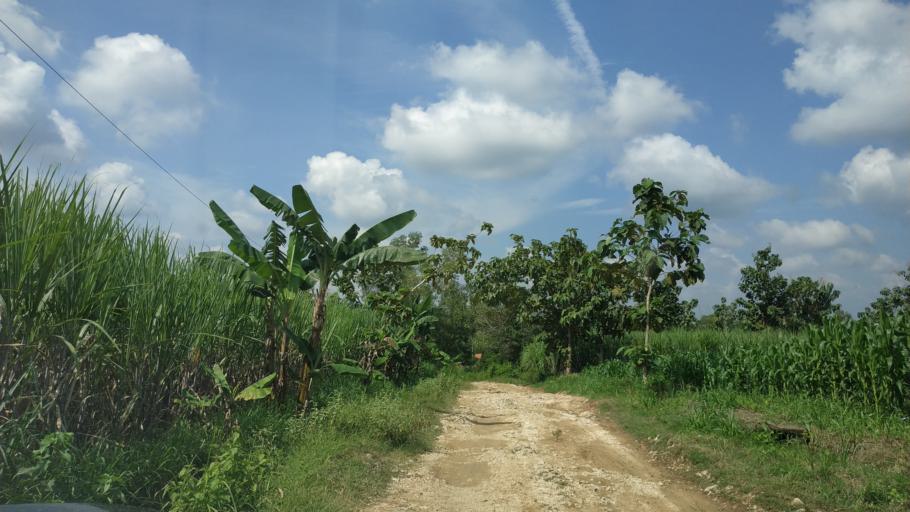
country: ID
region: Central Java
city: Guyangan
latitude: -7.0066
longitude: 111.1009
